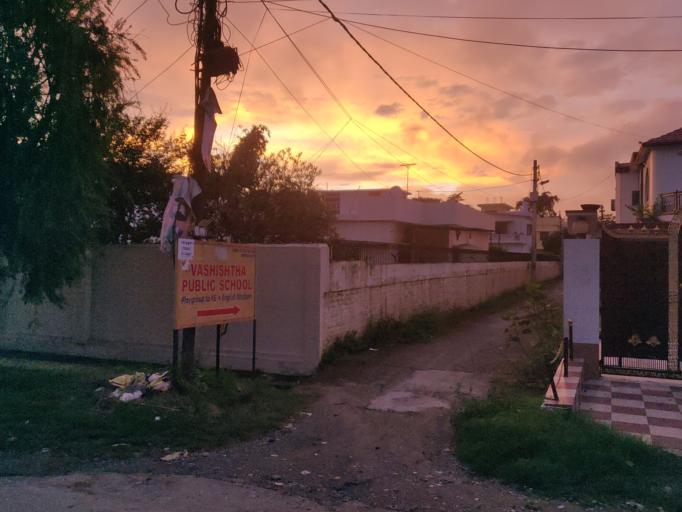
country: IN
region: Uttarakhand
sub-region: Dehradun
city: Clement Town
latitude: 30.2971
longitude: 77.9978
